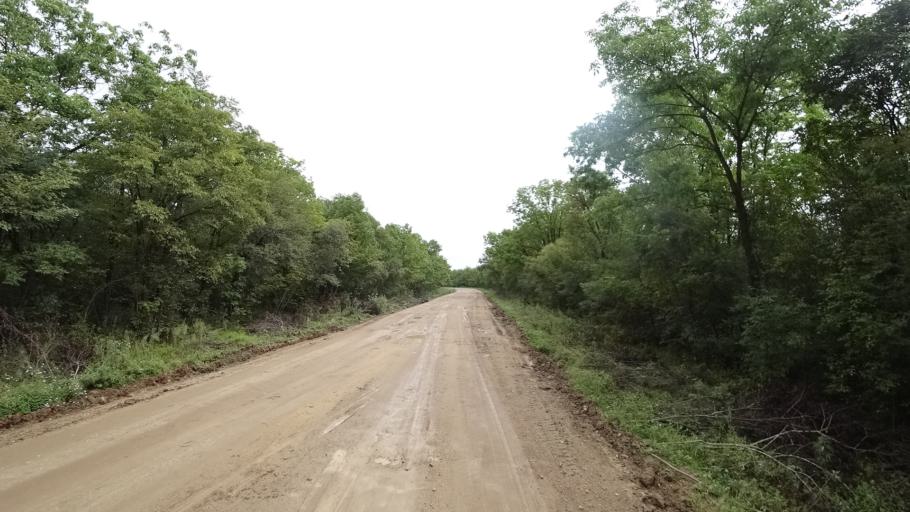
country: RU
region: Primorskiy
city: Lyalichi
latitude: 44.0778
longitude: 132.4548
